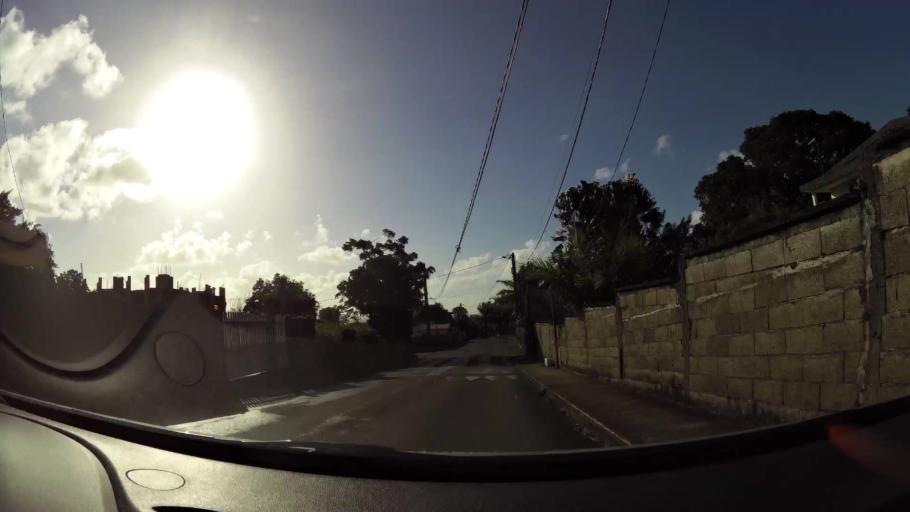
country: MQ
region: Martinique
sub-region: Martinique
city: Le Lamentin
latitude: 14.6249
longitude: -61.0245
